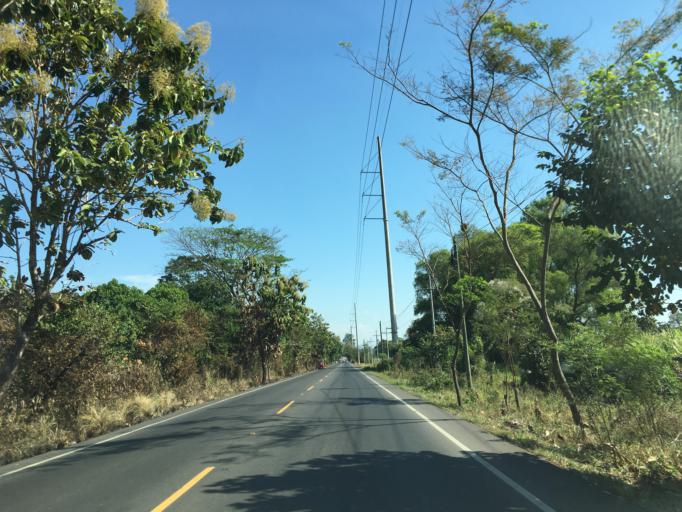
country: GT
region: Escuintla
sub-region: Municipio de La Democracia
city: La Democracia
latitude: 14.2177
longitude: -90.9533
